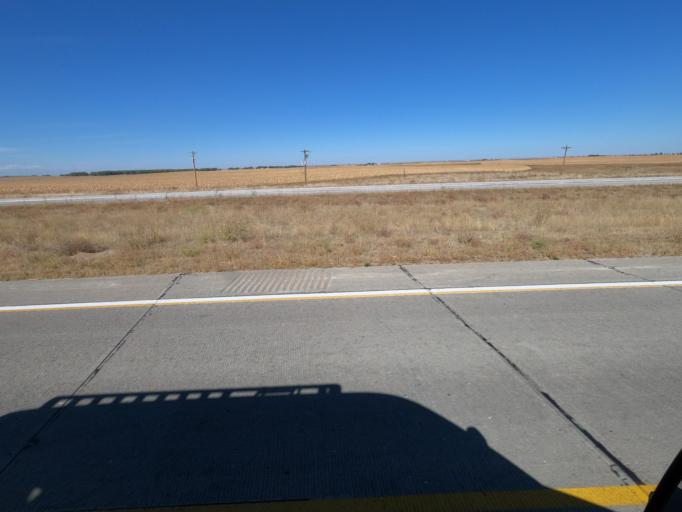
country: US
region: Colorado
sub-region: Morgan County
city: Fort Morgan
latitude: 40.2321
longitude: -104.1339
